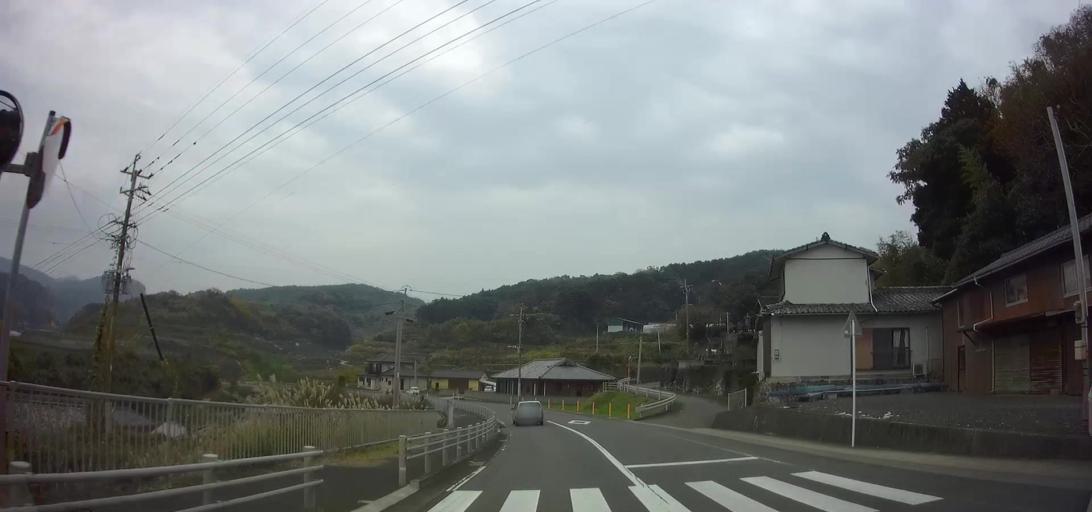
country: JP
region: Nagasaki
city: Shimabara
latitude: 32.7051
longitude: 130.1880
